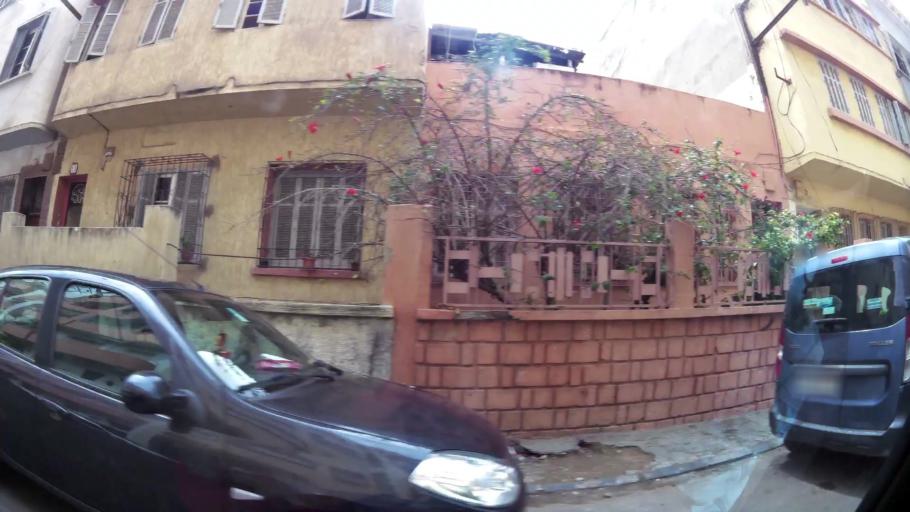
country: MA
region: Grand Casablanca
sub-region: Casablanca
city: Casablanca
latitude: 33.5965
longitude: -7.6418
